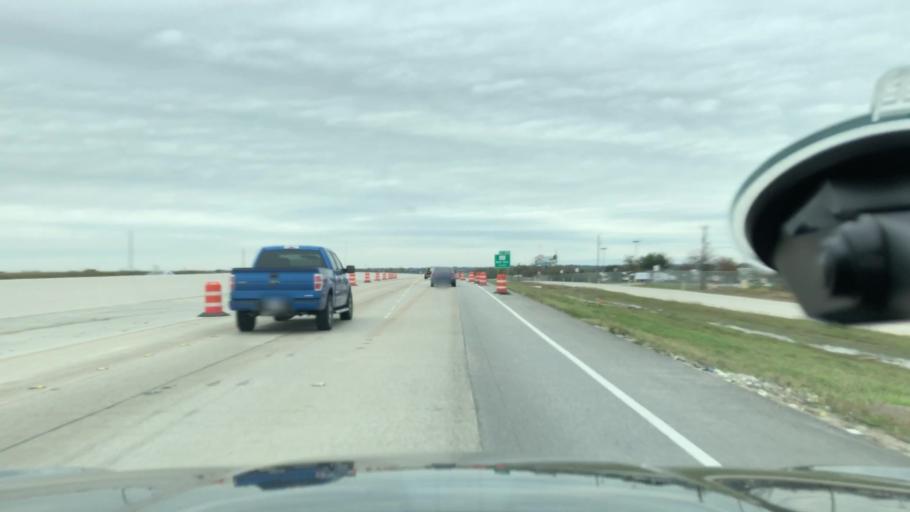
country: US
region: Texas
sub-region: Ellis County
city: Red Oak
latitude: 32.4821
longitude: -96.8314
